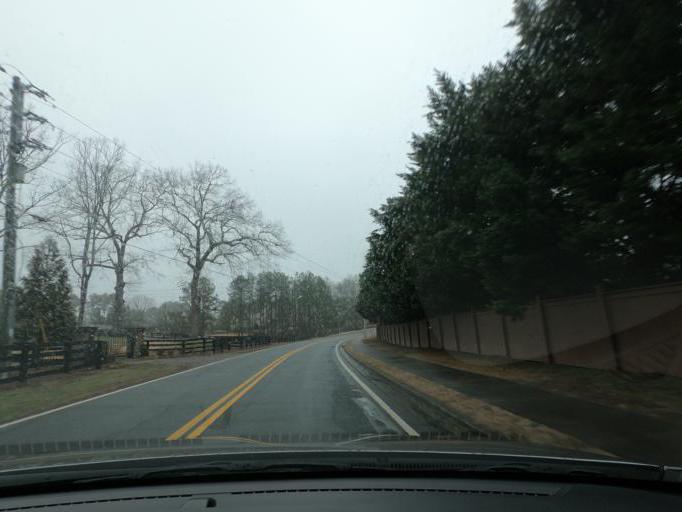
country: US
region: Georgia
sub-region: Fulton County
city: Milton
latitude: 34.1425
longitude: -84.2709
